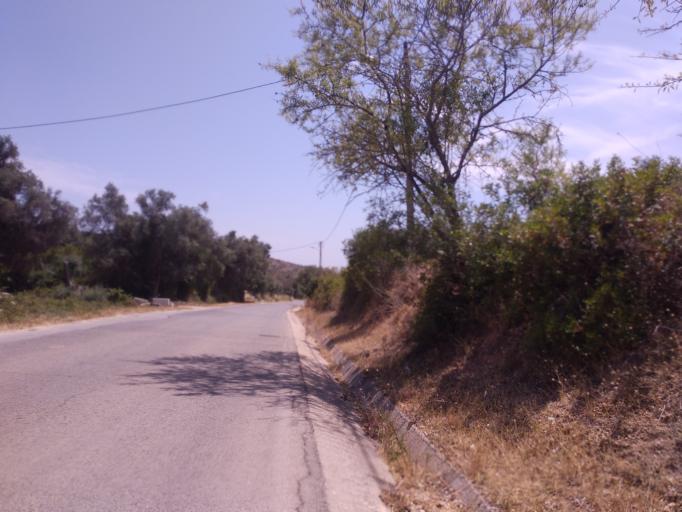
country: PT
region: Faro
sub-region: Faro
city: Santa Barbara de Nexe
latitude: 37.1144
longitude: -7.9456
